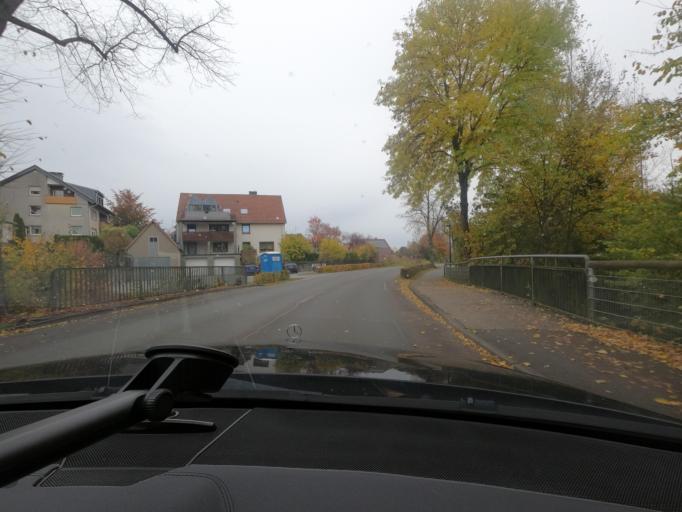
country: DE
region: North Rhine-Westphalia
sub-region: Regierungsbezirk Arnsberg
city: Mohnesee
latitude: 51.4948
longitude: 8.1281
